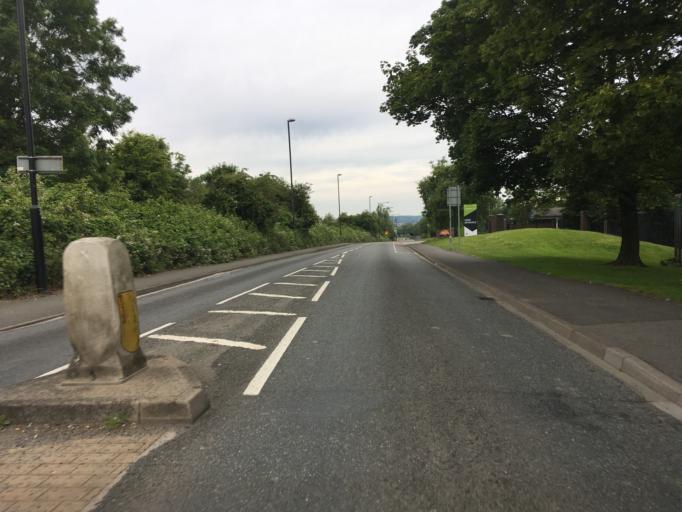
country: GB
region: England
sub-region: Bath and North East Somerset
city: Whitchurch
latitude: 51.4088
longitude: -2.5814
